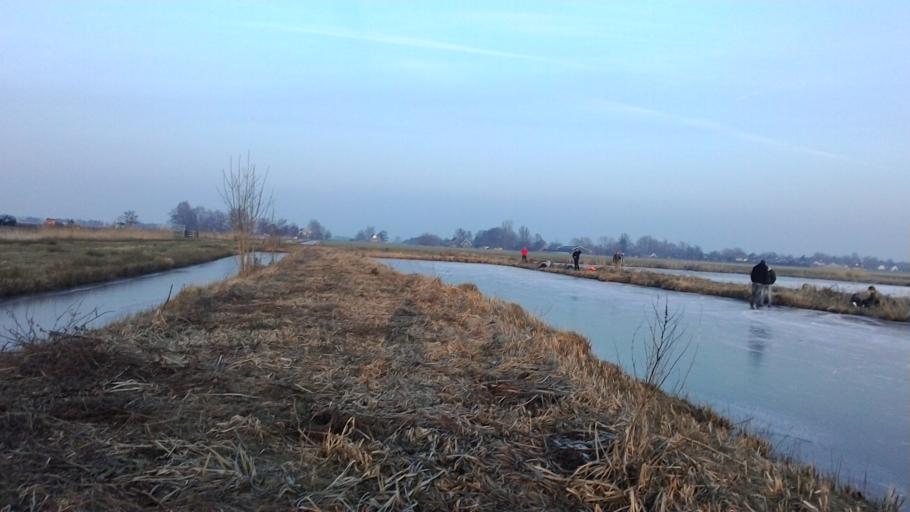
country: NL
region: North Holland
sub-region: Gemeente Wijdemeren
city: Oud-Loosdrecht
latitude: 52.1551
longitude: 5.0965
